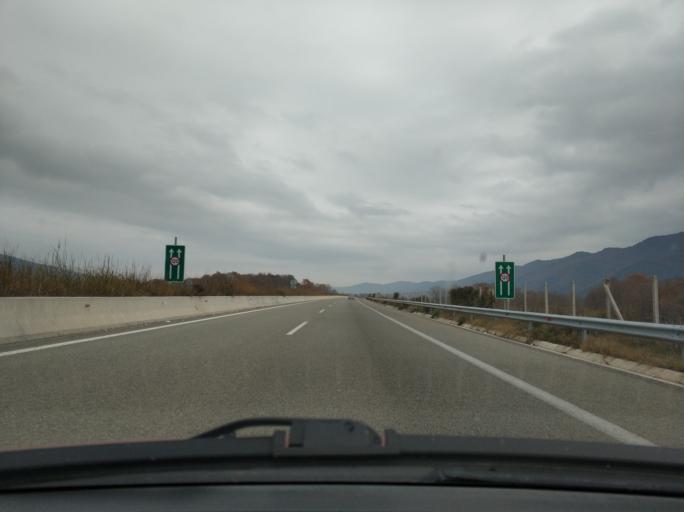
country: GR
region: East Macedonia and Thrace
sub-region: Nomos Kavalas
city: Palaiochori
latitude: 40.8595
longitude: 24.1657
